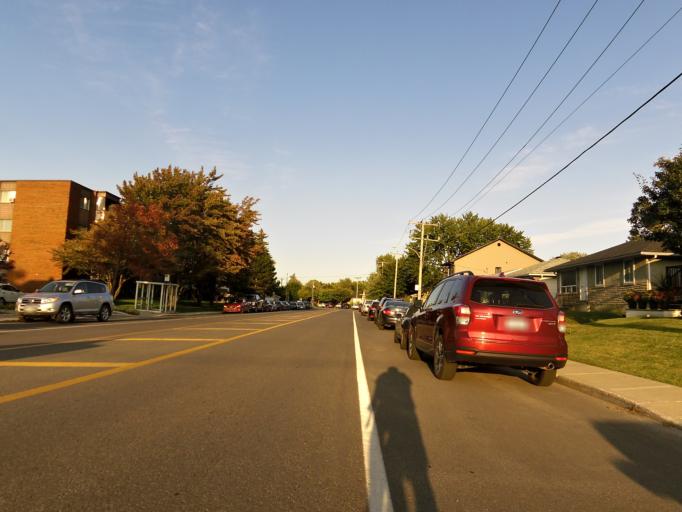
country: CA
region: Quebec
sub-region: Outaouais
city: Gatineau
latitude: 45.4676
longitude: -75.6901
